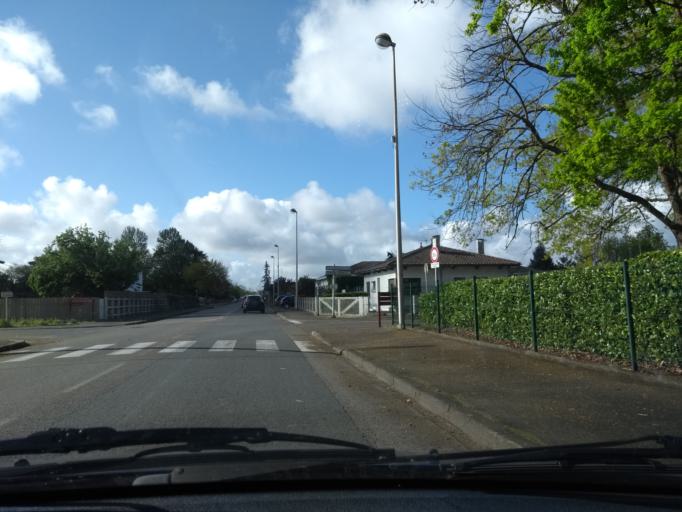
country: FR
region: Aquitaine
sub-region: Departement des Landes
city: Parentis-en-Born
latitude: 44.3543
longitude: -1.0738
